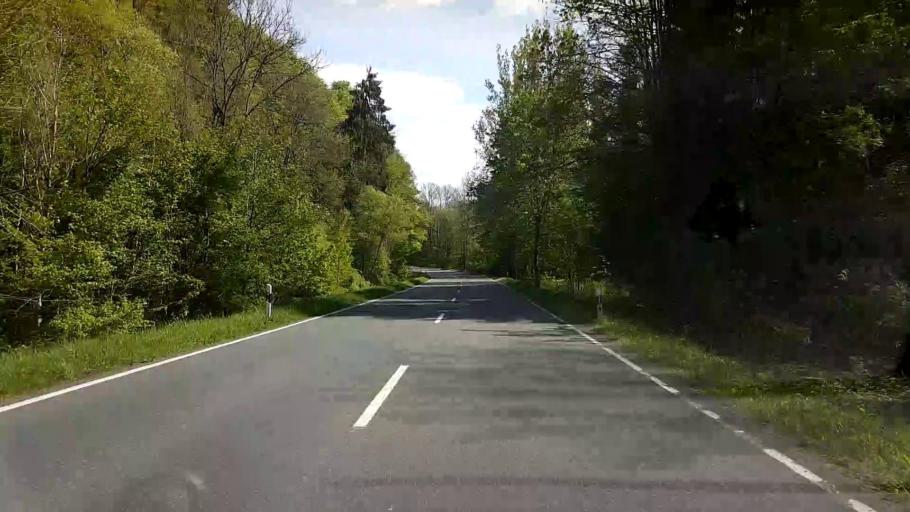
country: DE
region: Bavaria
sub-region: Upper Franconia
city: Ebermannstadt
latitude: 49.8017
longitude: 11.1677
